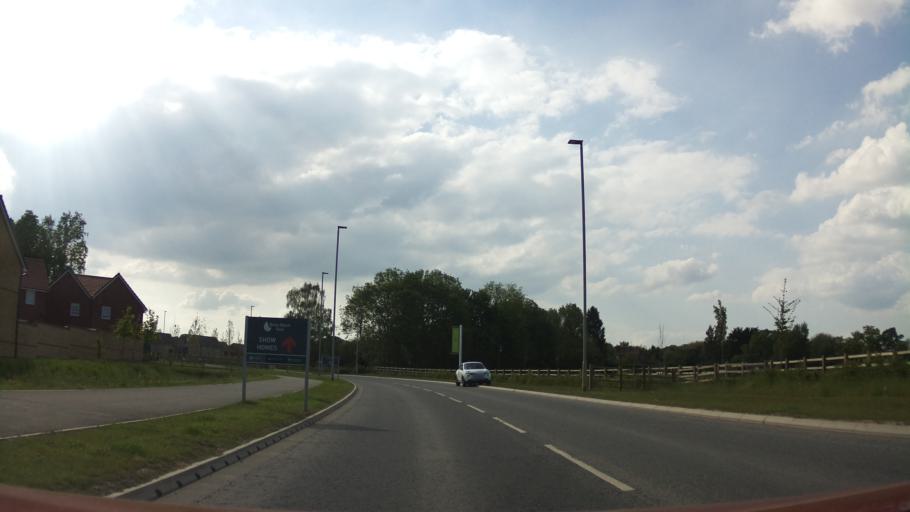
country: GB
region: England
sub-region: Wiltshire
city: Chippenham
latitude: 51.4740
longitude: -2.1105
